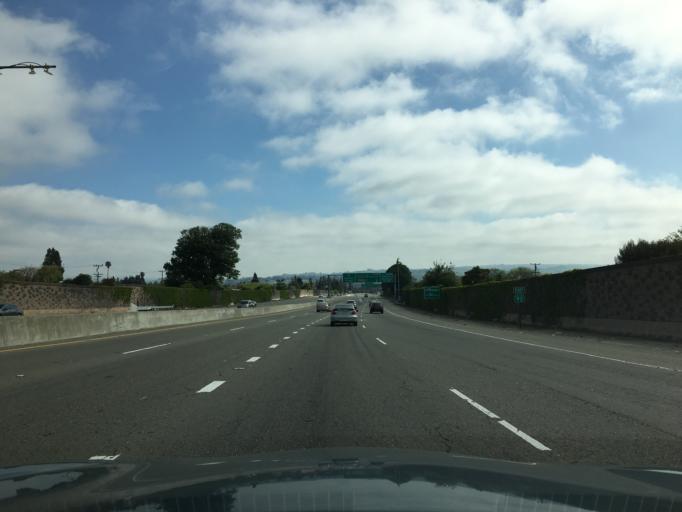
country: US
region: California
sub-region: Alameda County
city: Hayward
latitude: 37.6325
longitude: -122.1093
